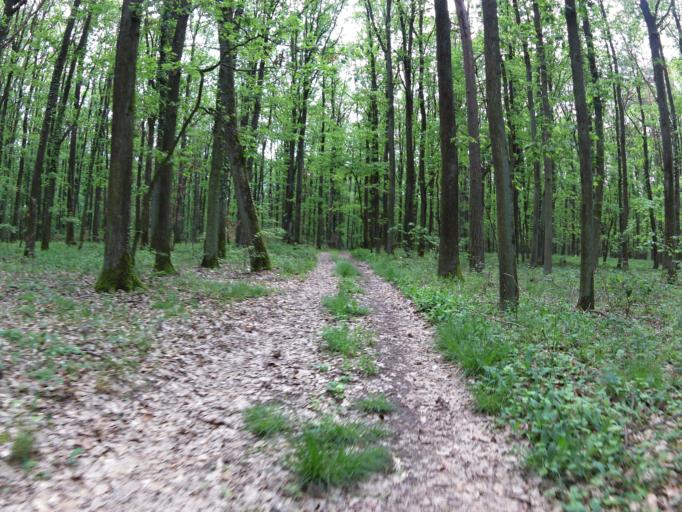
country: DE
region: Bavaria
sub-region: Regierungsbezirk Unterfranken
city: Sommerhausen
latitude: 49.7168
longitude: 10.0306
